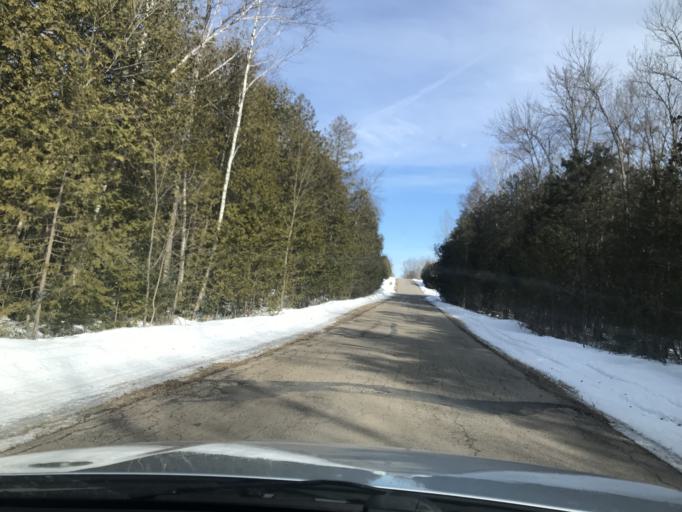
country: US
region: Wisconsin
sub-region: Oconto County
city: Gillett
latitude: 44.9603
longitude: -88.2753
